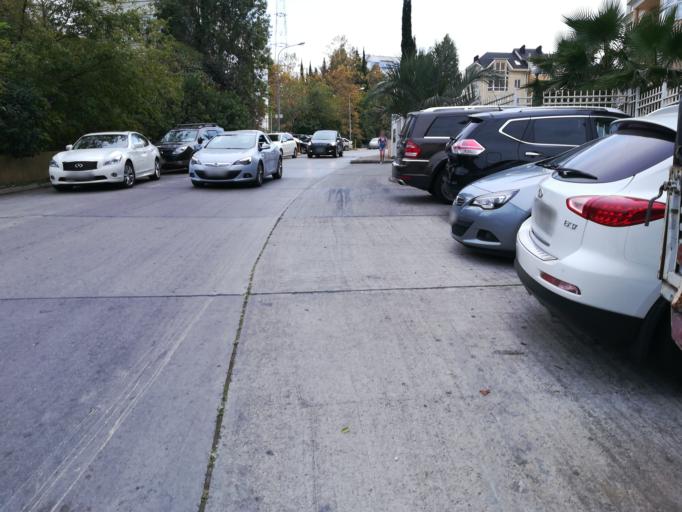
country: RU
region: Krasnodarskiy
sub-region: Sochi City
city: Sochi
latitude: 43.5926
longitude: 39.7349
